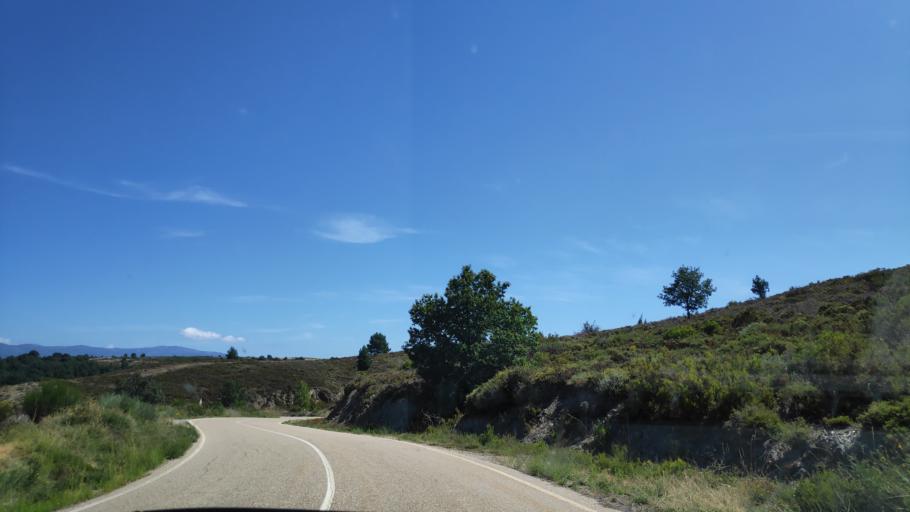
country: ES
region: Castille and Leon
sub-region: Provincia de Zamora
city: Requejo
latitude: 42.0209
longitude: -6.6980
